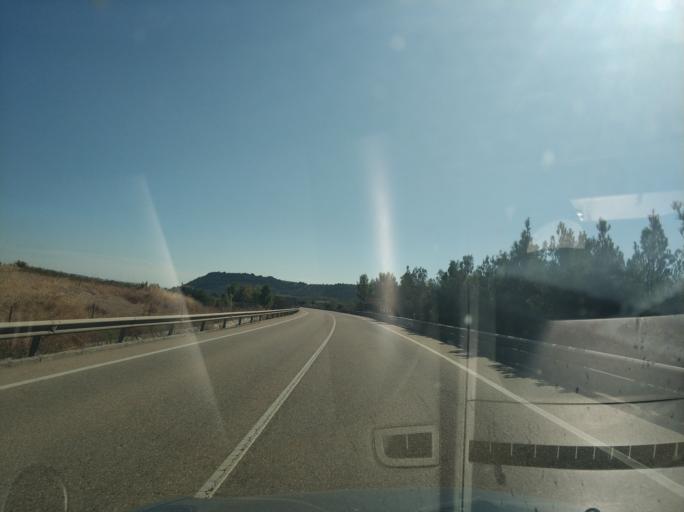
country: ES
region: Castille and Leon
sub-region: Provincia de Valladolid
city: Quintanilla de Arriba
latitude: 41.6178
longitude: -4.2236
